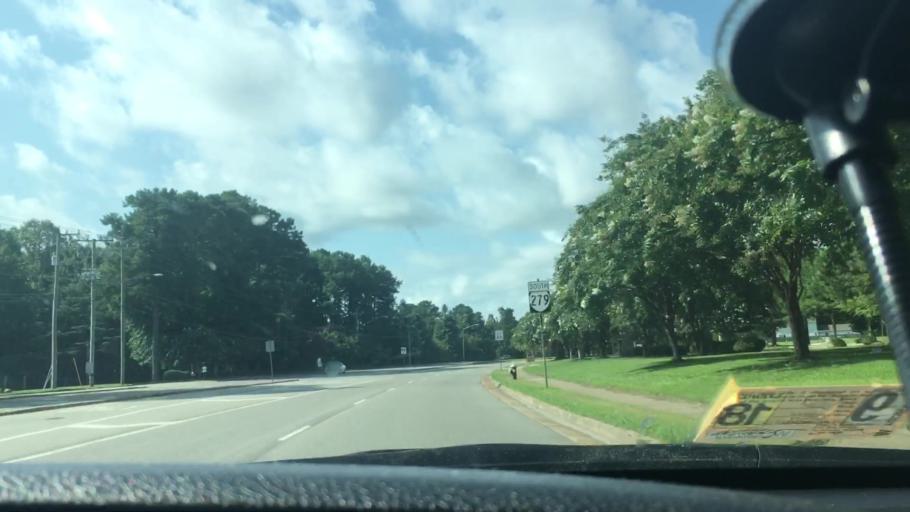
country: US
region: Virginia
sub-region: City of Virginia Beach
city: Virginia Beach
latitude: 36.8733
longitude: -76.0398
